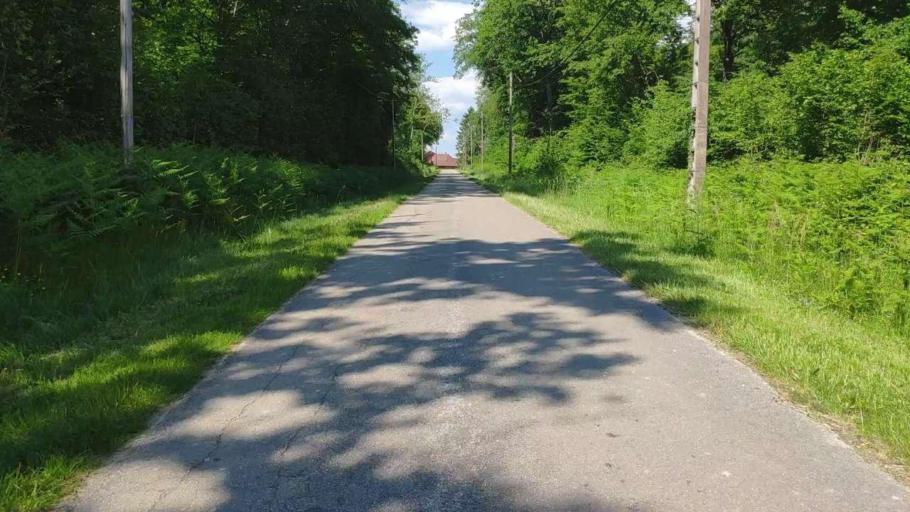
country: FR
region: Franche-Comte
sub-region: Departement du Jura
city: Bletterans
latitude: 46.8165
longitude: 5.4081
